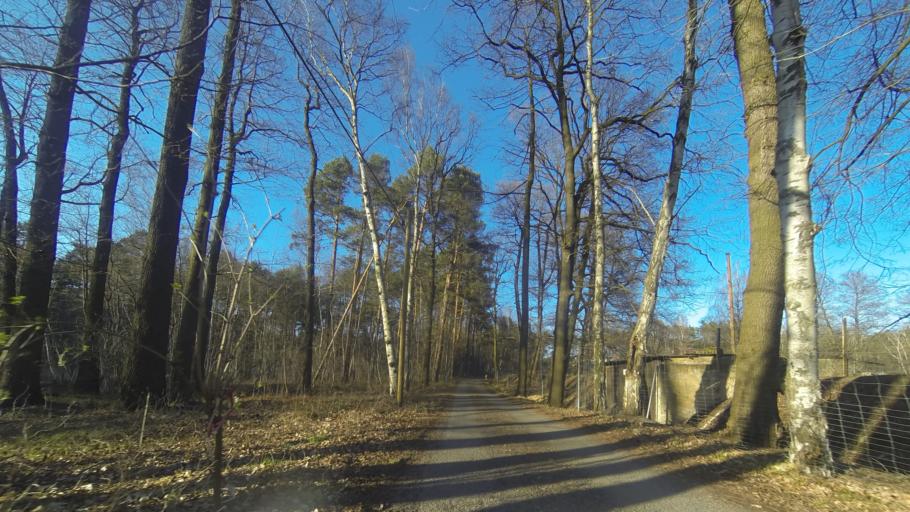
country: DE
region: Saxony
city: Ottendorf-Okrilla
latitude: 51.1950
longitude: 13.7969
